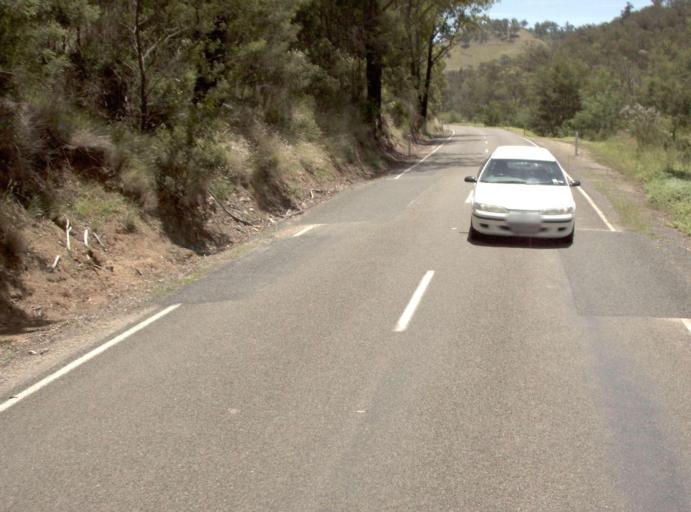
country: AU
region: Victoria
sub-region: East Gippsland
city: Bairnsdale
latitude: -37.4918
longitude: 147.8338
